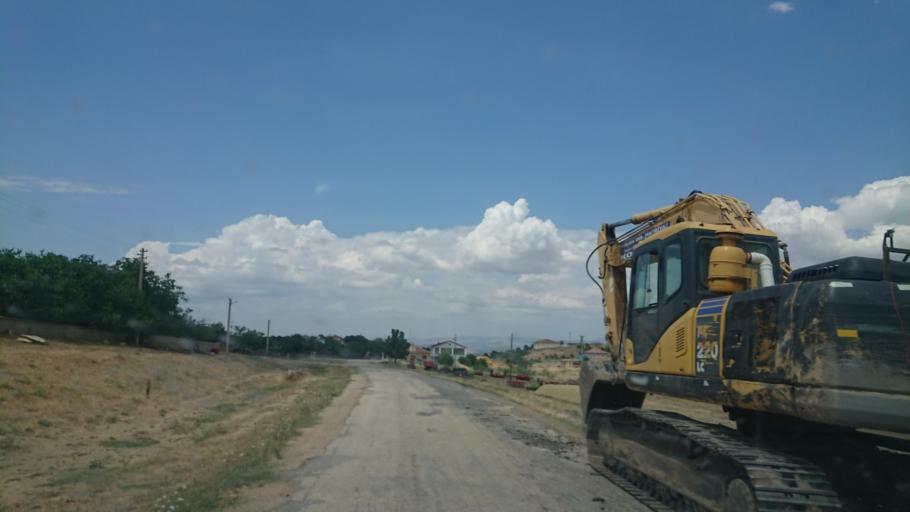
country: TR
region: Aksaray
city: Sariyahsi
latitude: 38.9537
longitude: 33.8832
